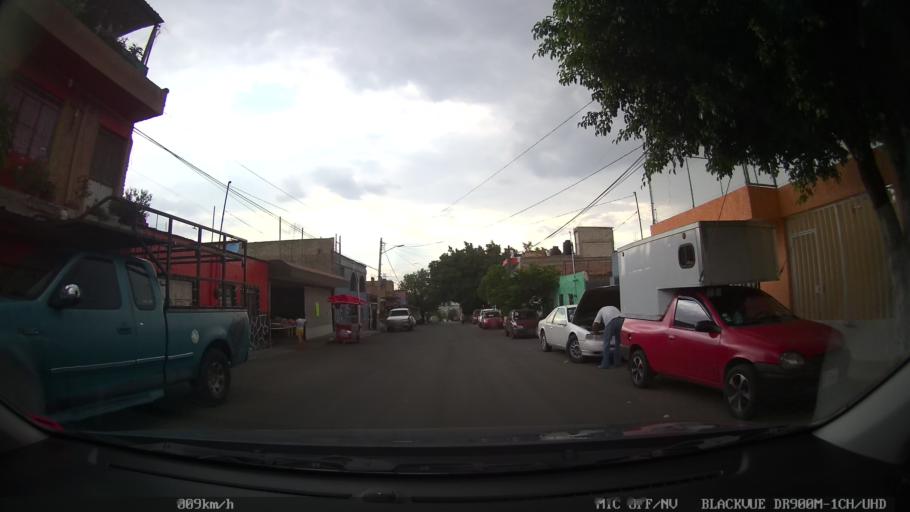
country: MX
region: Jalisco
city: Tlaquepaque
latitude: 20.6289
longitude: -103.2766
